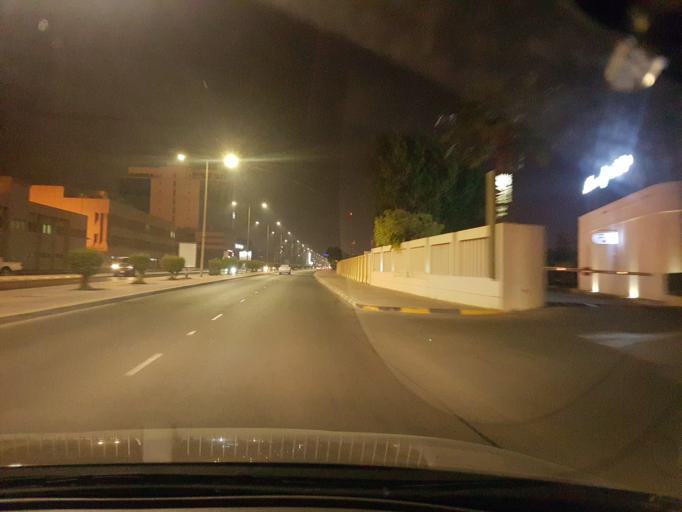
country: BH
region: Manama
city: Manama
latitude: 26.2082
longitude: 50.5951
